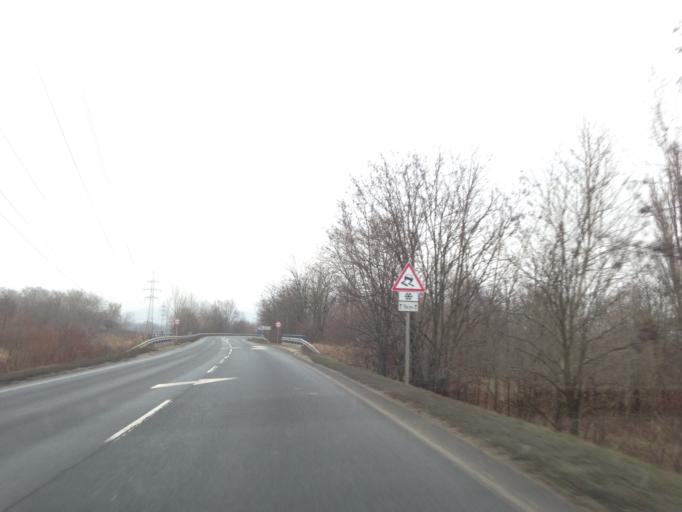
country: HU
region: Komarom-Esztergom
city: Szomod
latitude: 47.6764
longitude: 18.3209
